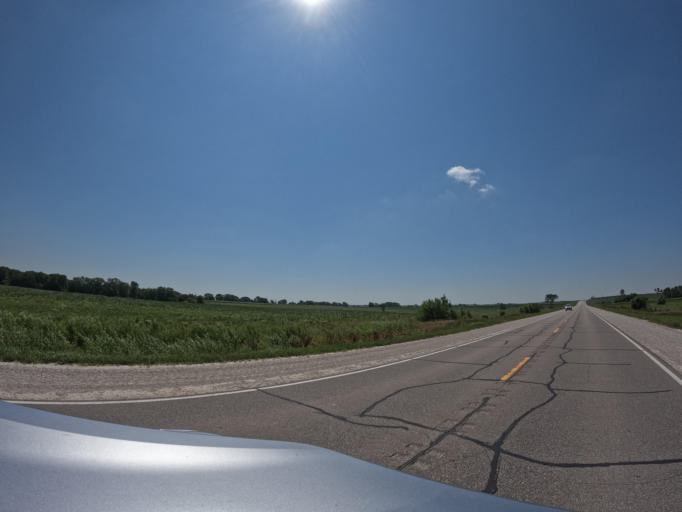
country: US
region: Iowa
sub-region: Keokuk County
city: Sigourney
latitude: 41.2969
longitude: -92.2047
